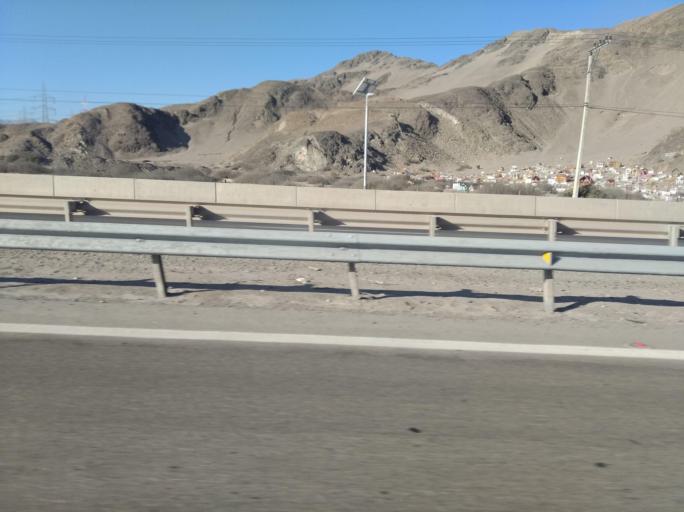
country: CL
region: Atacama
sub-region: Provincia de Copiapo
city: Copiapo
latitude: -27.3223
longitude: -70.3974
